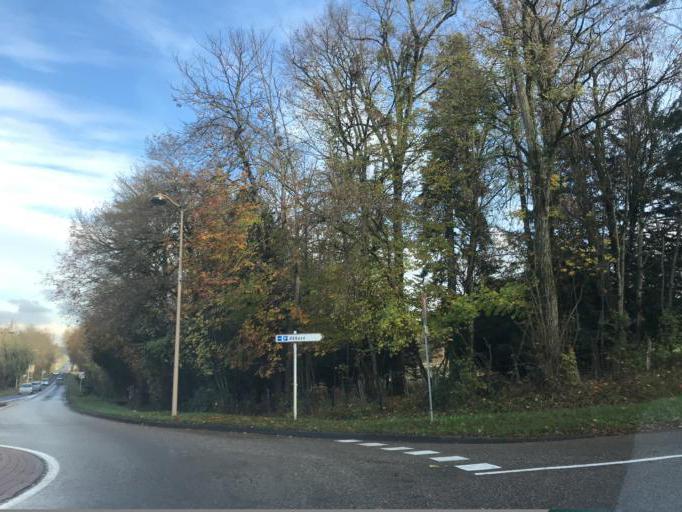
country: FR
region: Rhone-Alpes
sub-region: Departement de l'Ain
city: Ambronay
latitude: 46.0087
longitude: 5.3620
